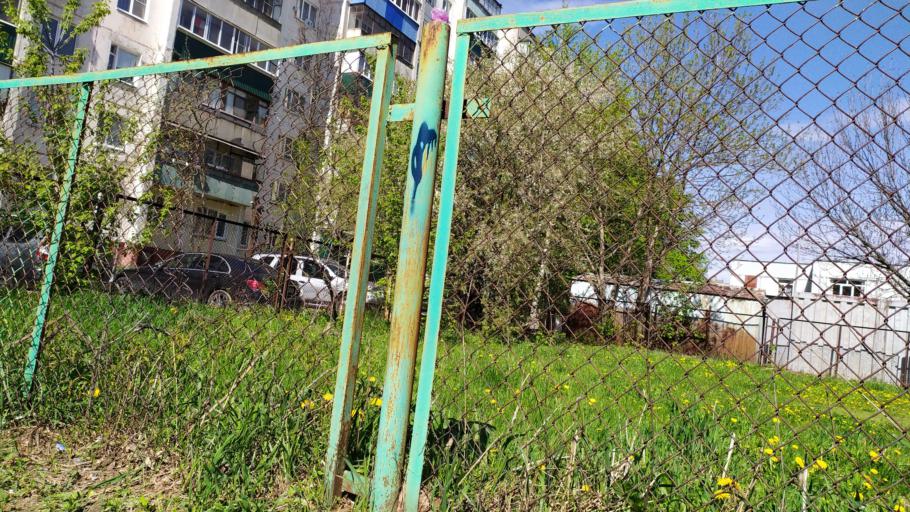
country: RU
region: Kursk
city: Kursk
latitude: 51.7402
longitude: 36.1362
